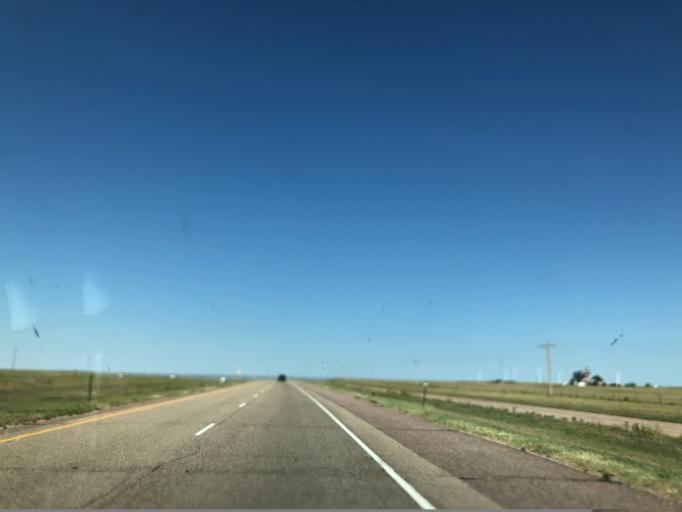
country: US
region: Colorado
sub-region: Lincoln County
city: Hugo
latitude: 39.2742
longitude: -103.5026
